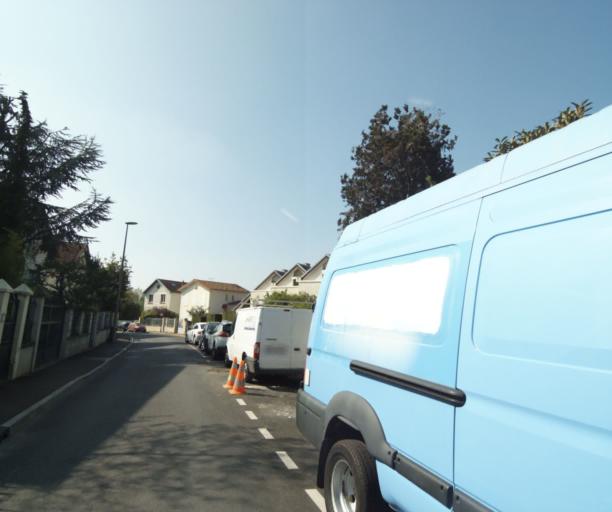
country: FR
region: Ile-de-France
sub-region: Departement des Hauts-de-Seine
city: Sevres
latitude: 48.8196
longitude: 2.2107
